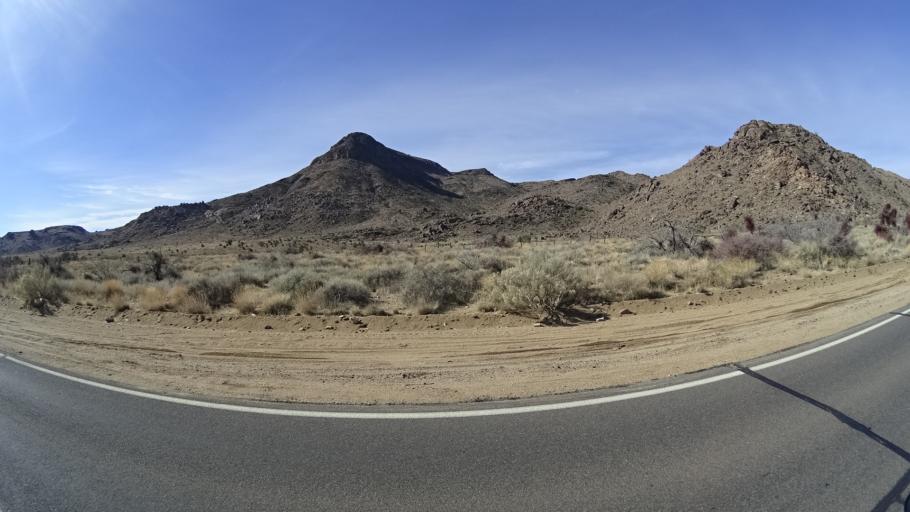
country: US
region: Arizona
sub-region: Mohave County
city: New Kingman-Butler
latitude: 35.2863
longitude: -114.0562
